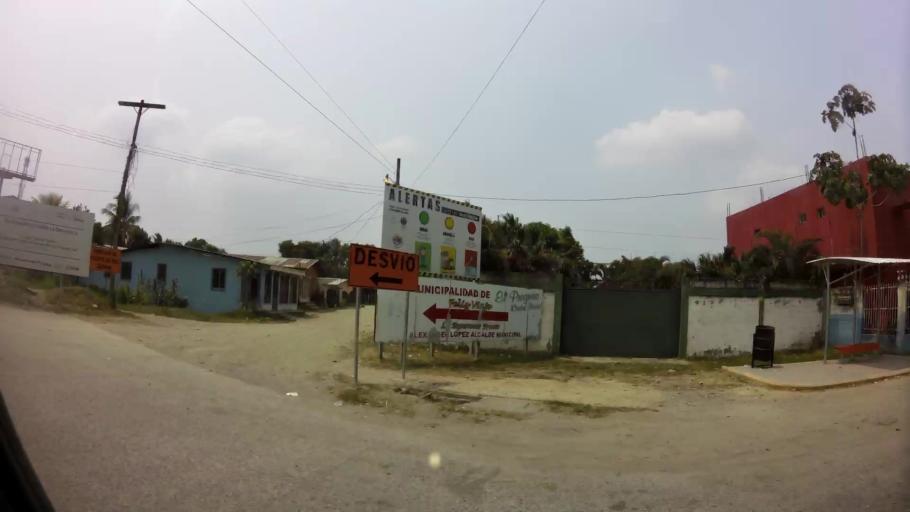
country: HN
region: Yoro
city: El Progreso
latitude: 15.4031
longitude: -87.8166
